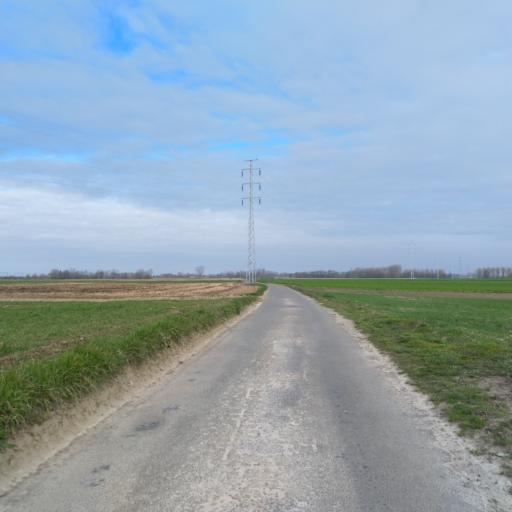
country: BE
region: Wallonia
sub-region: Province du Hainaut
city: Lens
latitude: 50.5679
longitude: 3.9035
